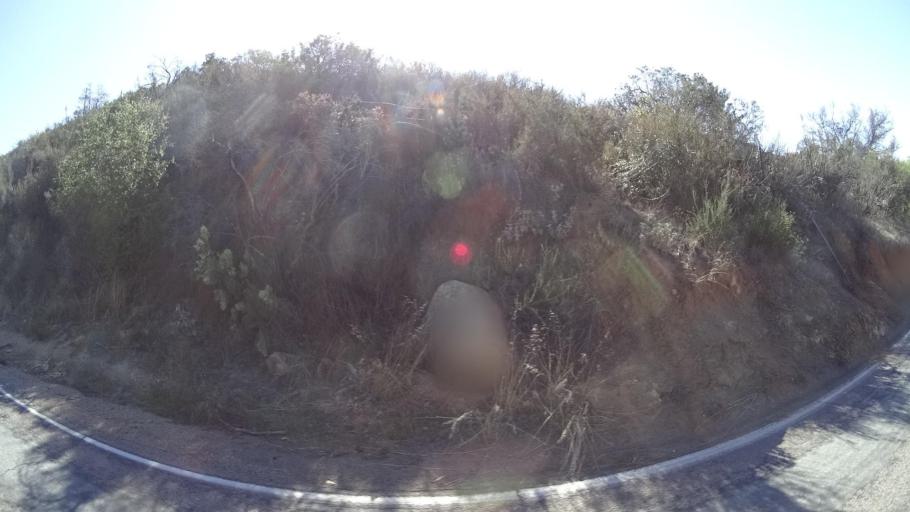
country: US
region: California
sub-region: San Diego County
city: Jamul
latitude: 32.7088
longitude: -116.7877
